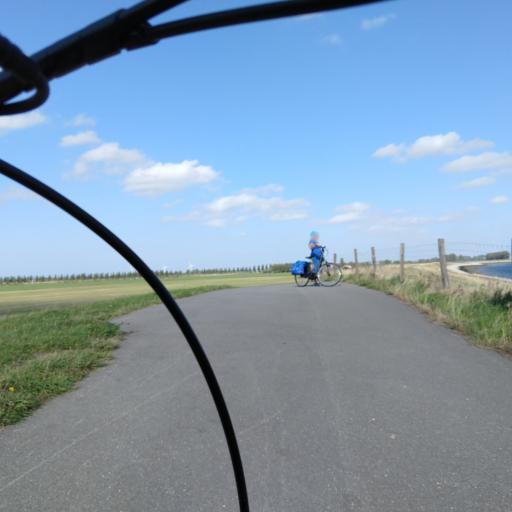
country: NL
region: Zeeland
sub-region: Gemeente Goes
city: Goes
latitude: 51.5475
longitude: 3.8648
